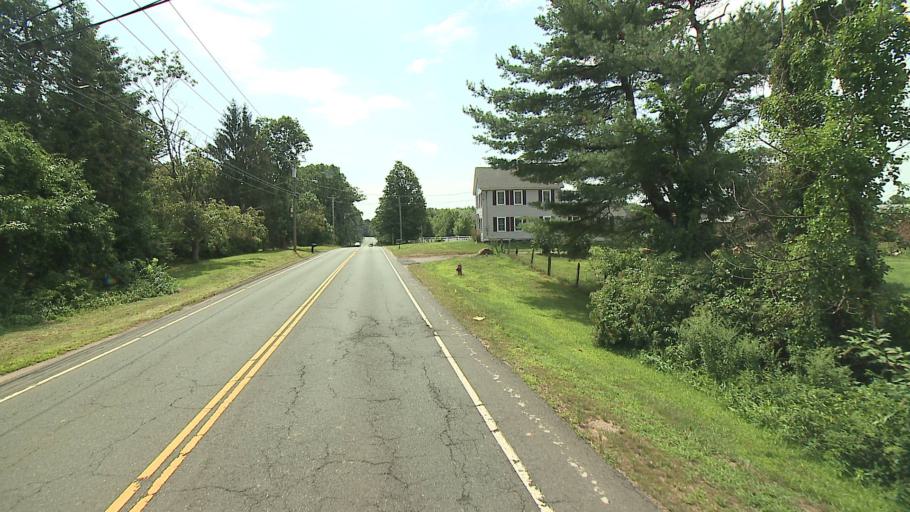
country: US
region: Connecticut
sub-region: Hartford County
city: Farmington
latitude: 41.7272
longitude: -72.8888
